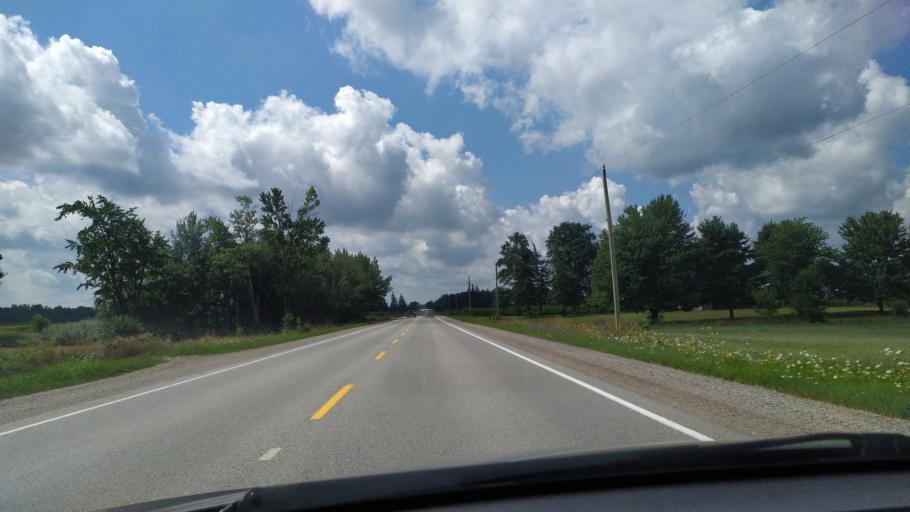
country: CA
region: Ontario
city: South Huron
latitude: 43.2875
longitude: -81.3440
